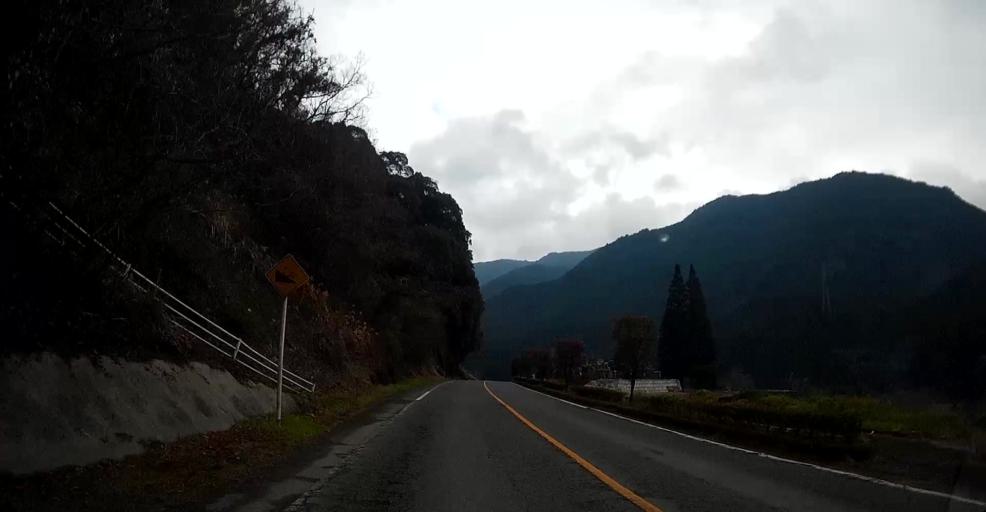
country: JP
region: Kumamoto
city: Matsubase
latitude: 32.6151
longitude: 130.8432
